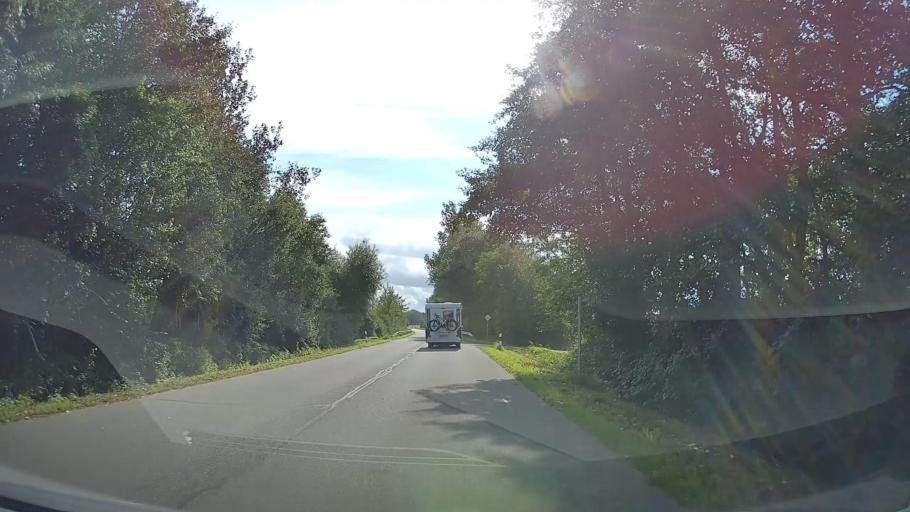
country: DE
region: Schleswig-Holstein
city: Glucksburg
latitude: 54.8603
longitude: 9.5888
